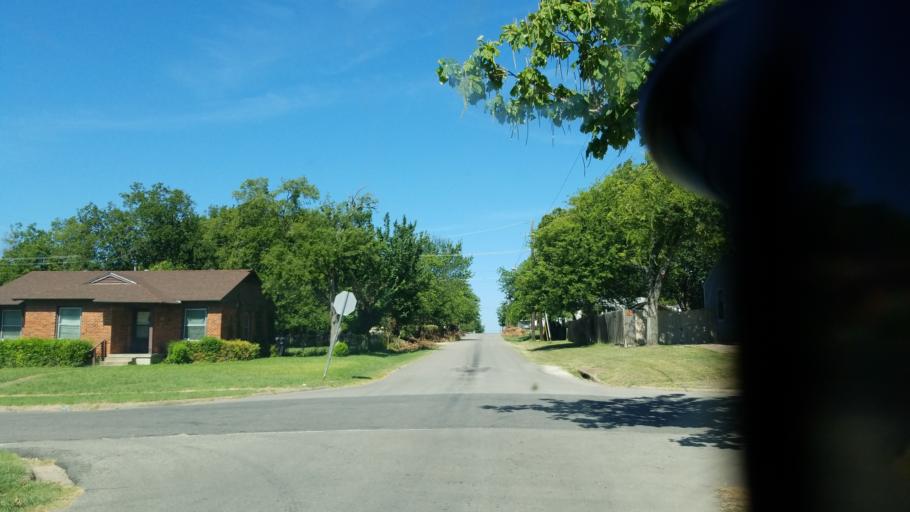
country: US
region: Texas
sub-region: Dallas County
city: Dallas
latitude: 32.7030
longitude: -96.8120
